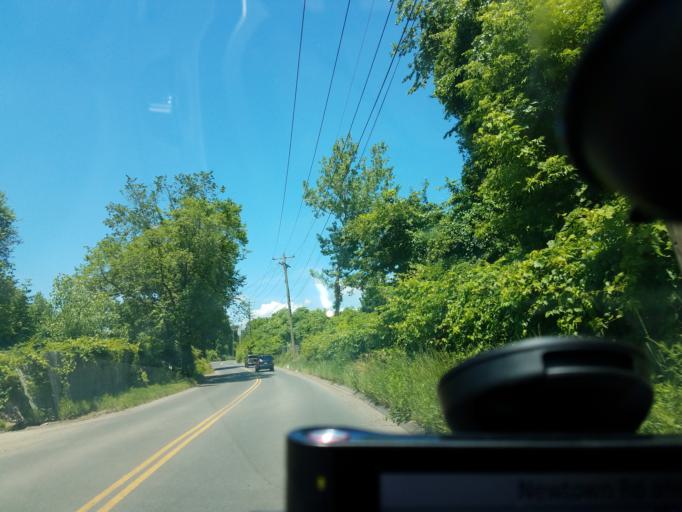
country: US
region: Connecticut
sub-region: Fairfield County
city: Bethel
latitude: 41.3989
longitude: -73.4137
